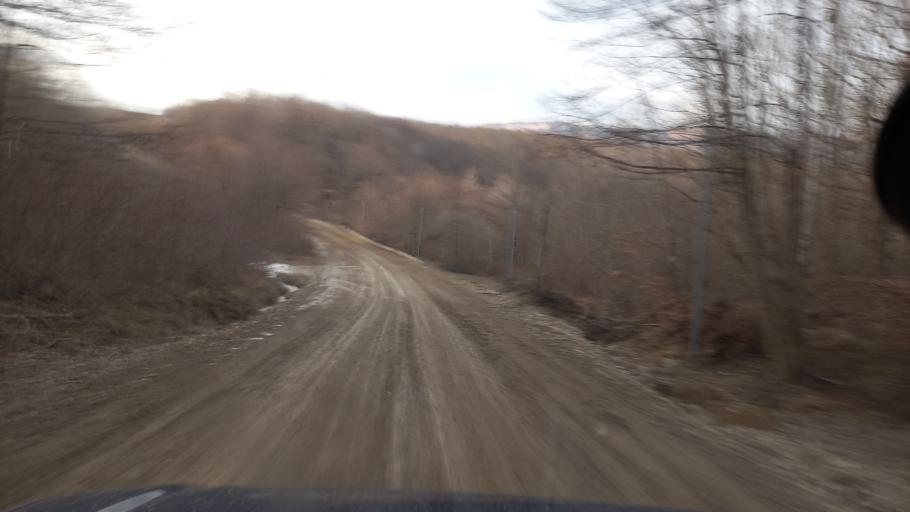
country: RU
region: Adygeya
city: Kamennomostskiy
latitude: 44.1924
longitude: 40.2594
